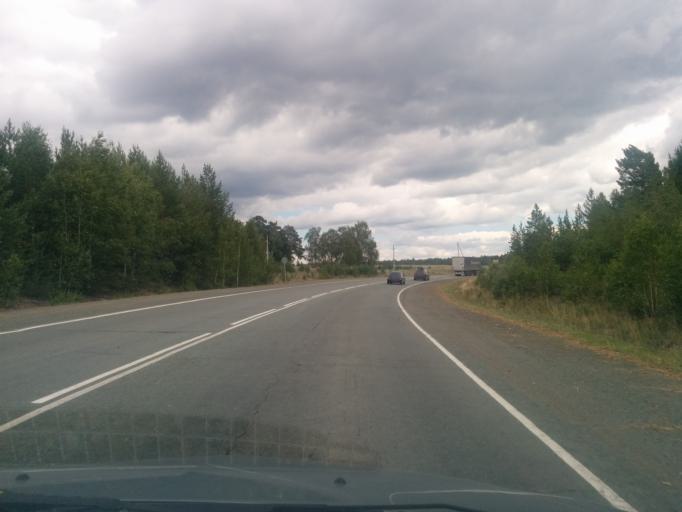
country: RU
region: Bashkortostan
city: Lomovka
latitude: 53.8959
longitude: 58.0901
